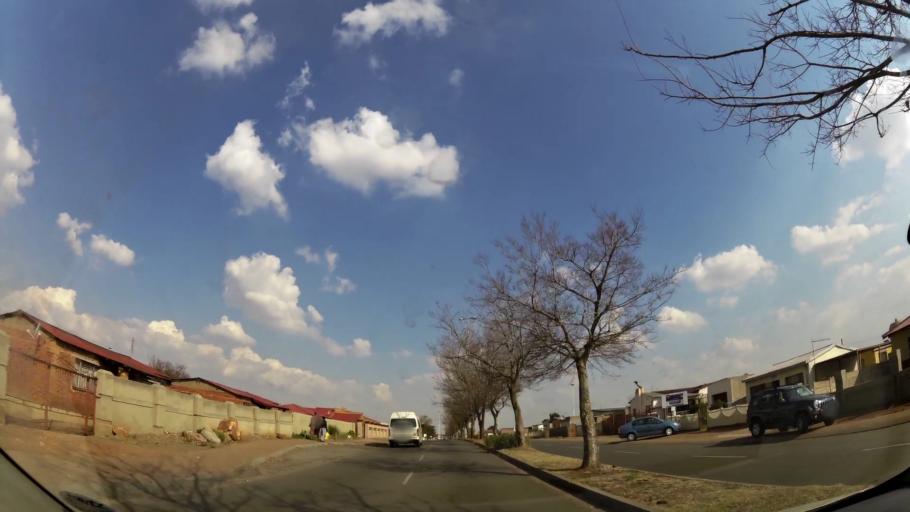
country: ZA
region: Gauteng
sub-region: Ekurhuleni Metropolitan Municipality
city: Germiston
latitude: -26.3187
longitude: 28.1579
